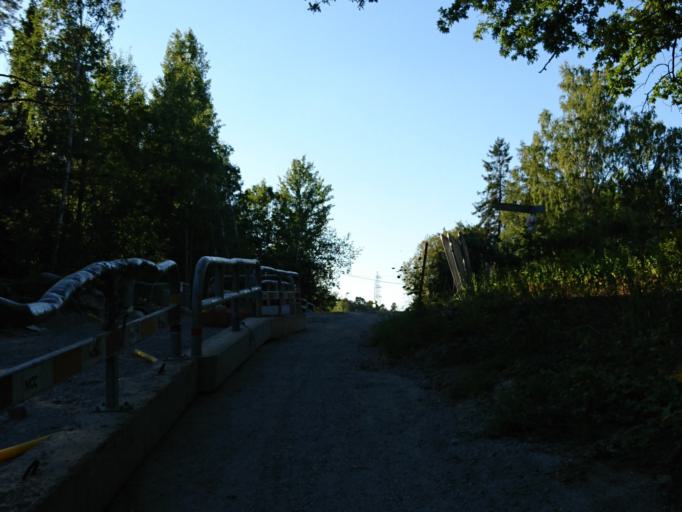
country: SE
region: Stockholm
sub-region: Huddinge Kommun
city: Segeltorp
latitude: 59.2709
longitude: 17.9237
